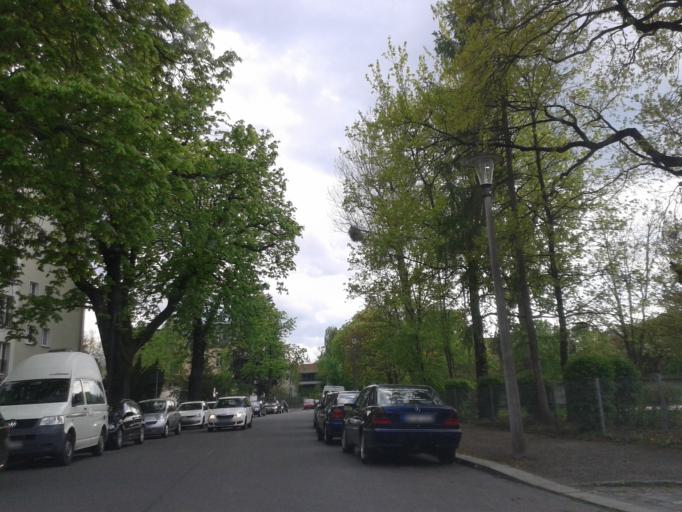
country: DE
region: Saxony
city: Dresden
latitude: 51.0356
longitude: 13.7541
